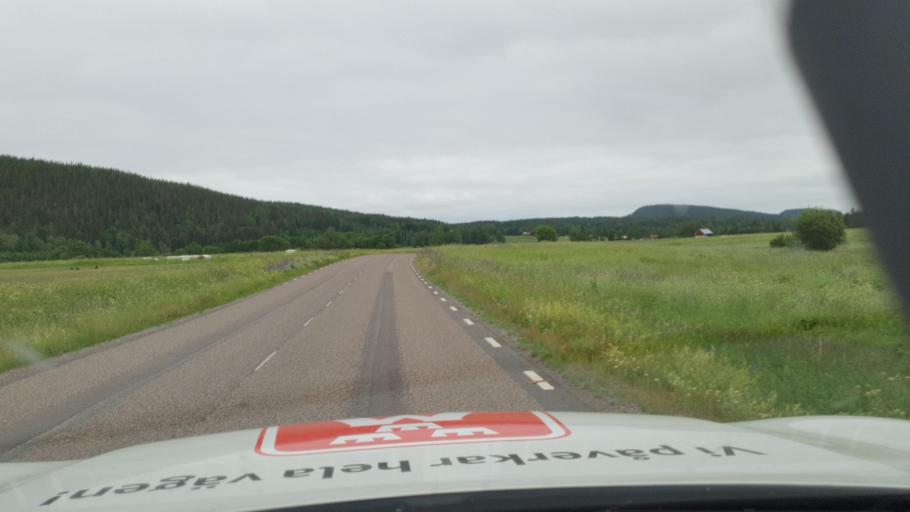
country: SE
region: Vaermland
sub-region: Sunne Kommun
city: Sunne
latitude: 59.8189
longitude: 13.2126
